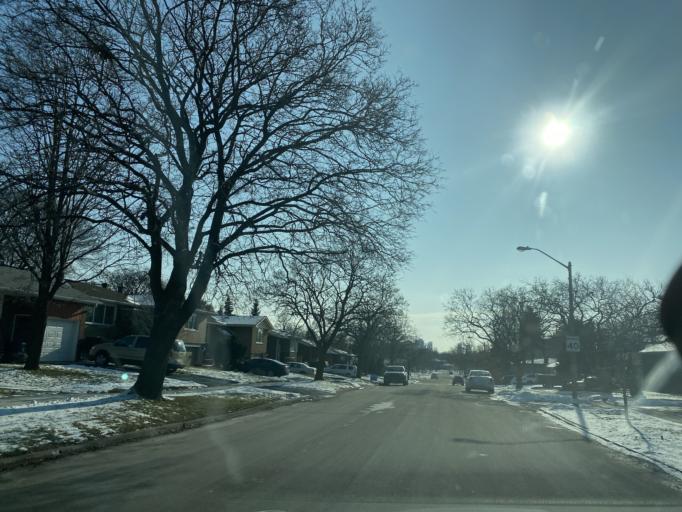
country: CA
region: Ontario
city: Etobicoke
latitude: 43.6681
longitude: -79.5720
